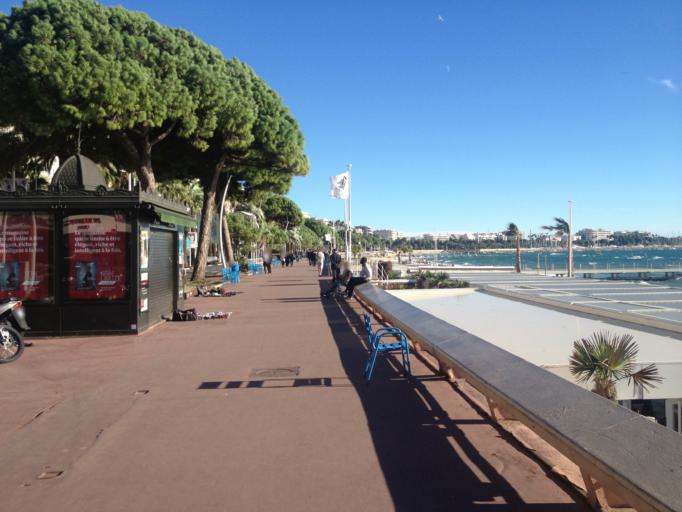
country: FR
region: Provence-Alpes-Cote d'Azur
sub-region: Departement des Alpes-Maritimes
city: Cannes
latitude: 43.5496
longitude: 7.0257
